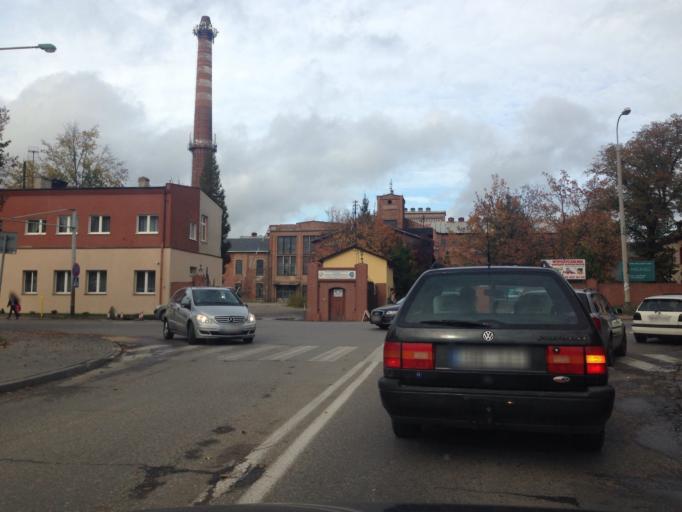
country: PL
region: Pomeranian Voivodeship
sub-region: Powiat gdanski
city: Pruszcz Gdanski
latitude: 54.2610
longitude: 18.6441
